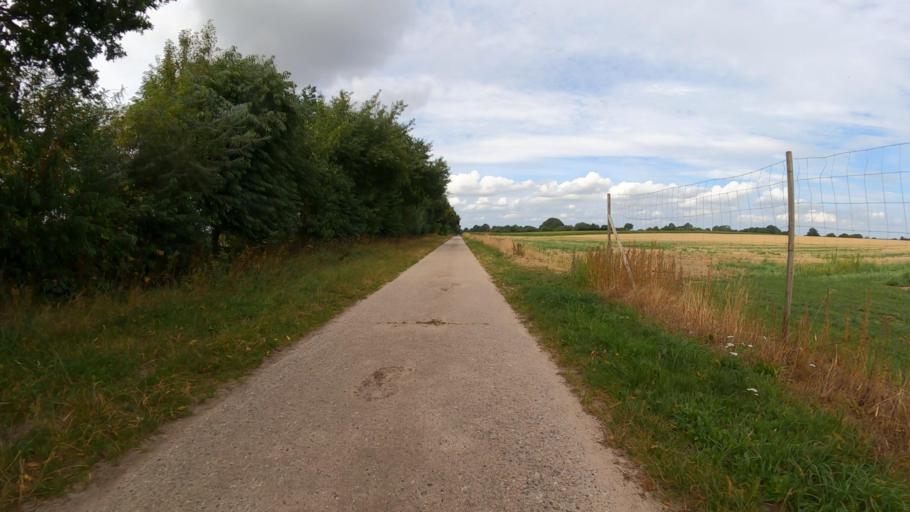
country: DE
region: Lower Saxony
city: Neu Wulmstorf
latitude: 53.4308
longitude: 9.8153
